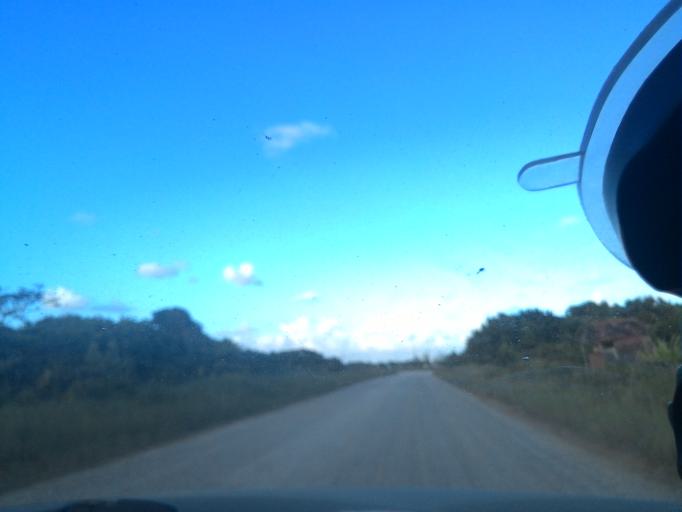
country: BR
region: Sao Paulo
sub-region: Iguape
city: Iguape
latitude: -24.8518
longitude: -47.7000
